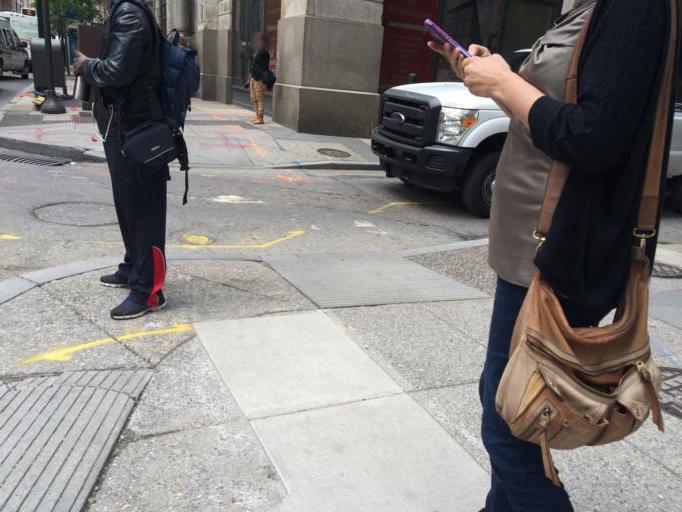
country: US
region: Pennsylvania
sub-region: Philadelphia County
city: Philadelphia
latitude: 39.9491
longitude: -75.1631
